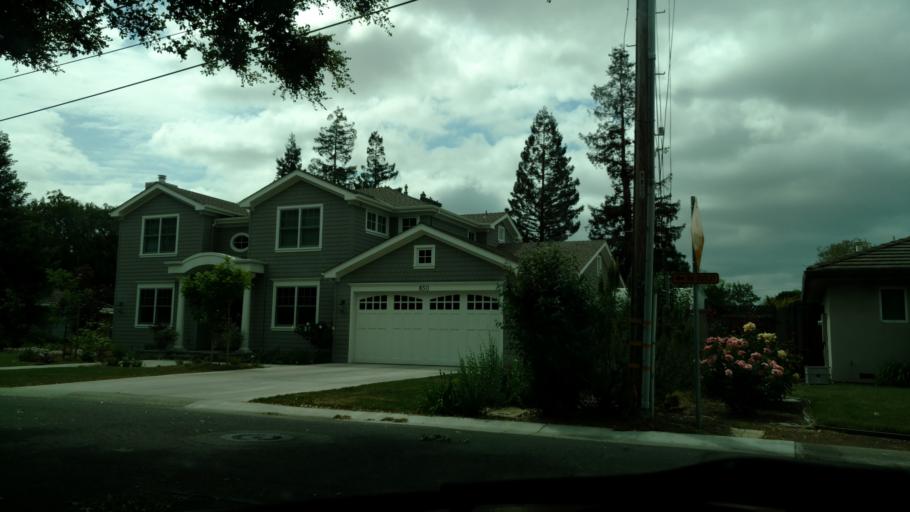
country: US
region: California
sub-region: Santa Clara County
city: Mountain View
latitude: 37.3820
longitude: -122.0905
